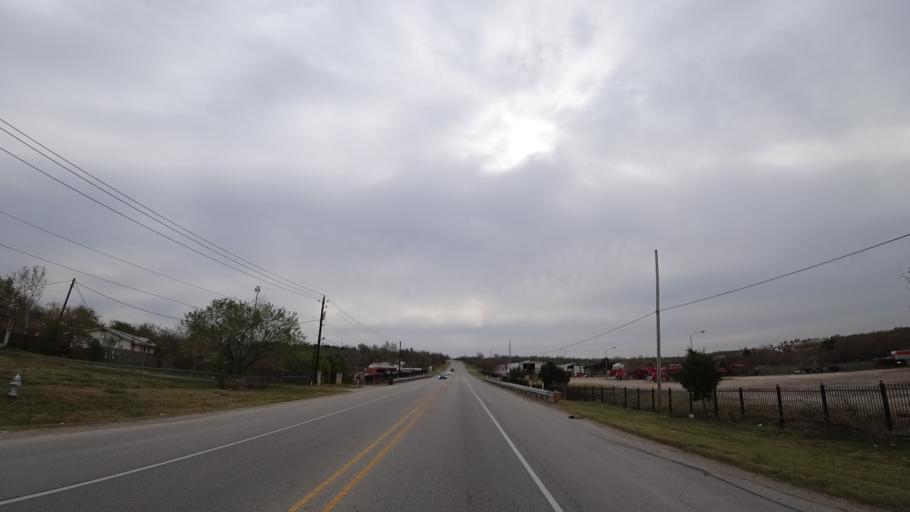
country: US
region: Texas
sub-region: Travis County
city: Garfield
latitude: 30.1291
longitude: -97.6432
